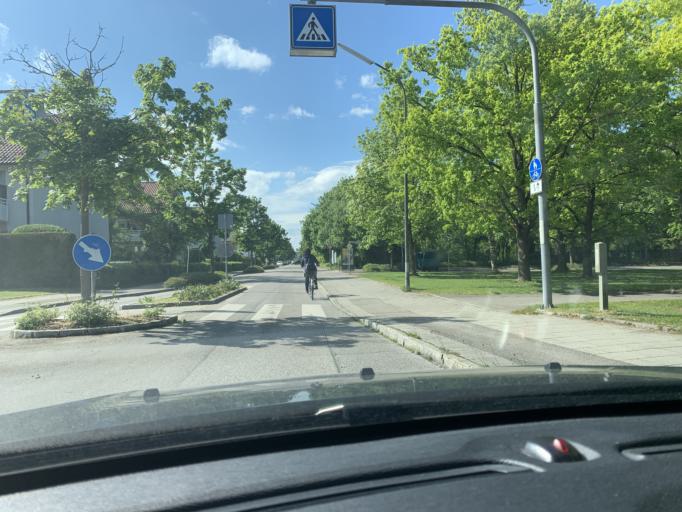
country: DE
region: Bavaria
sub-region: Upper Bavaria
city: Unterschleissheim
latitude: 48.2769
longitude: 11.5787
